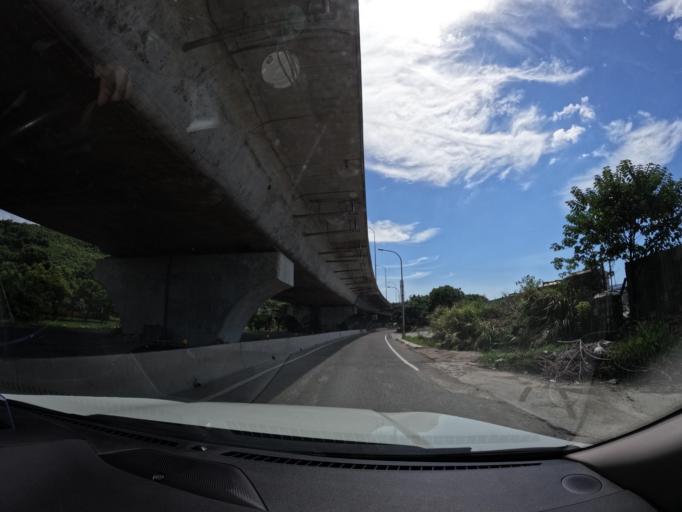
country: TW
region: Taipei
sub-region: Taipei
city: Banqiao
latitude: 25.1394
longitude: 121.3759
